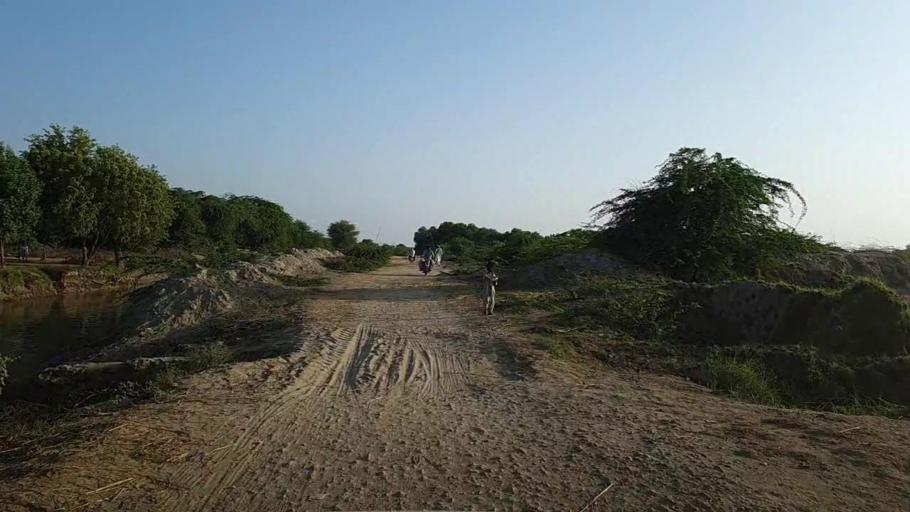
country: PK
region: Sindh
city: Kario
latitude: 24.7226
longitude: 68.6673
